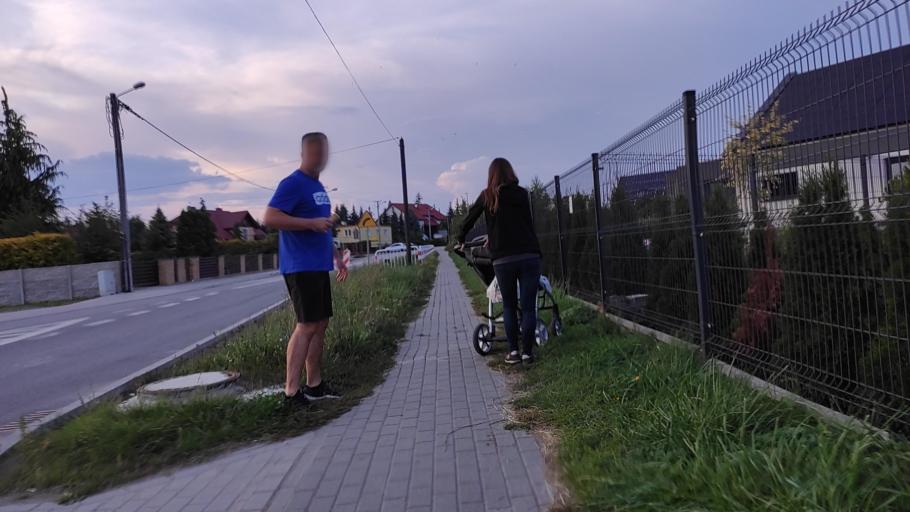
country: PL
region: Greater Poland Voivodeship
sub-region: Powiat poznanski
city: Kleszczewo
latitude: 52.3906
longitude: 17.1577
